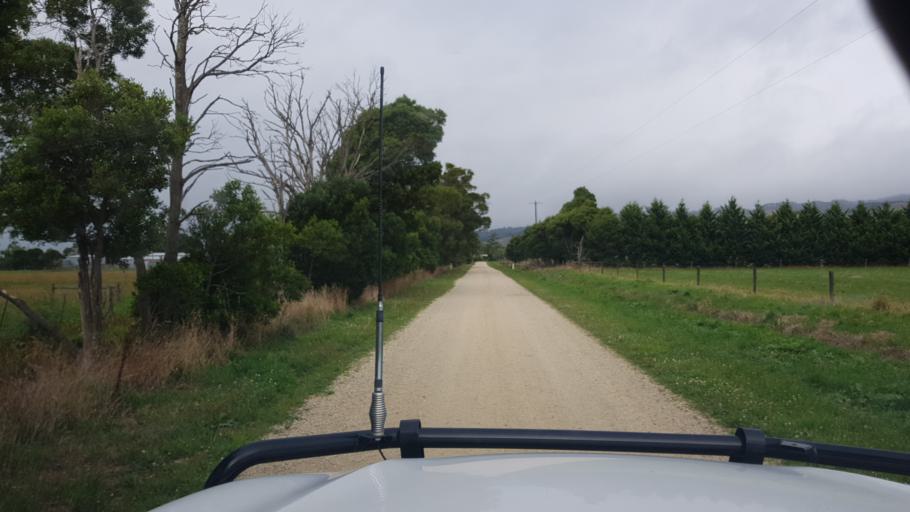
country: AU
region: Victoria
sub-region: Baw Baw
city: Warragul
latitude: -38.2309
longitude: 145.9933
